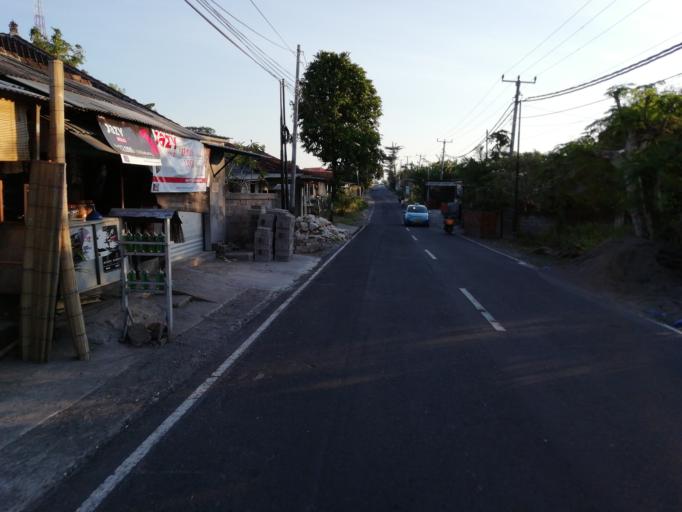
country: ID
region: Bali
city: Jimbaran
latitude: -8.8253
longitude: 115.1837
